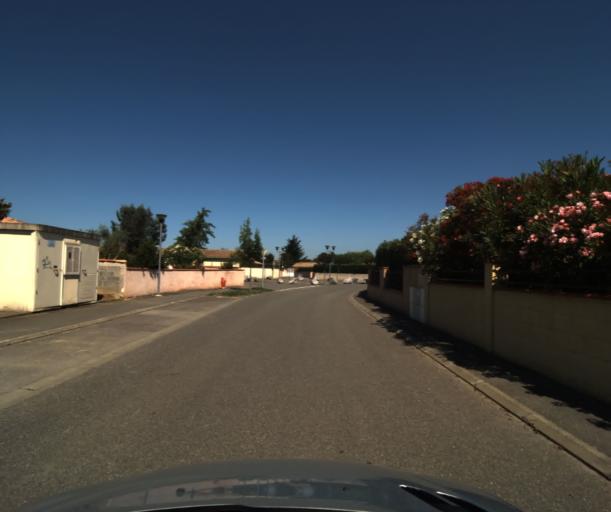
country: FR
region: Midi-Pyrenees
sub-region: Departement de la Haute-Garonne
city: Roquettes
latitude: 43.4992
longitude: 1.3717
